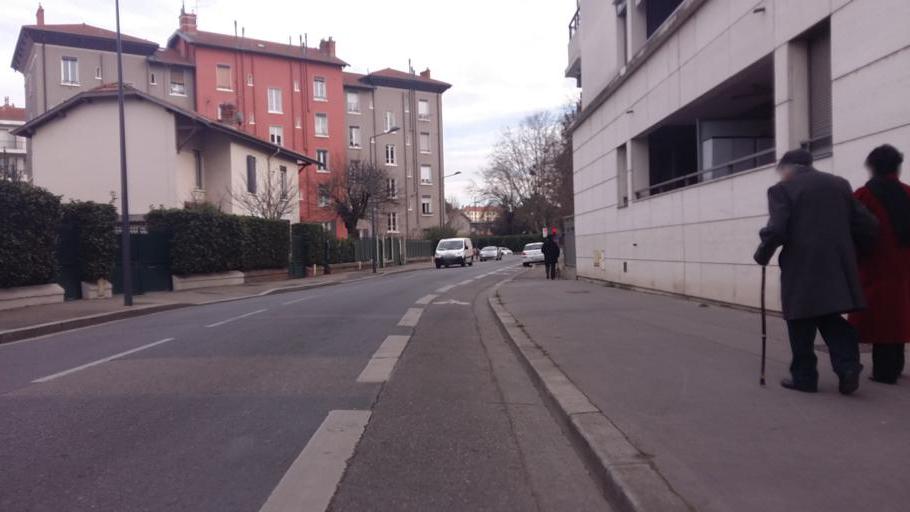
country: FR
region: Rhone-Alpes
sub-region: Departement du Rhone
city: Villeurbanne
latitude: 45.7705
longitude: 4.8889
